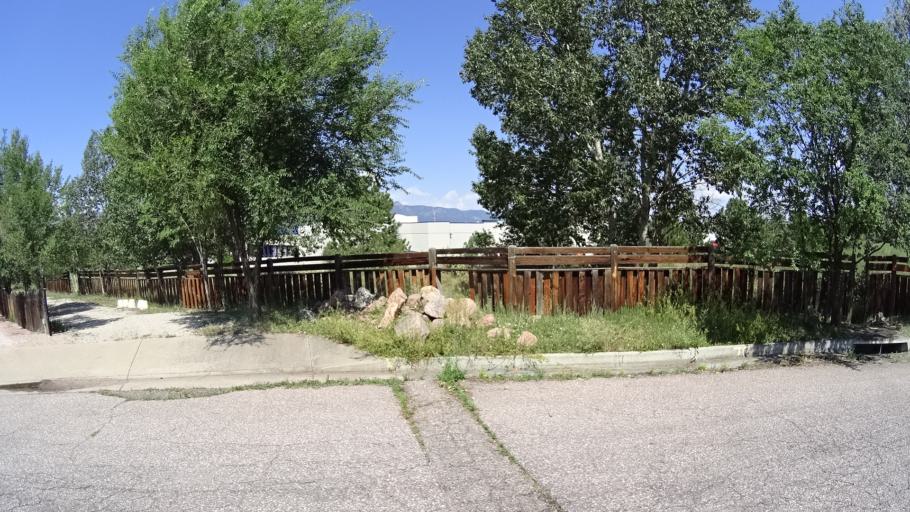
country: US
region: Colorado
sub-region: El Paso County
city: Air Force Academy
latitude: 38.9412
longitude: -104.7964
